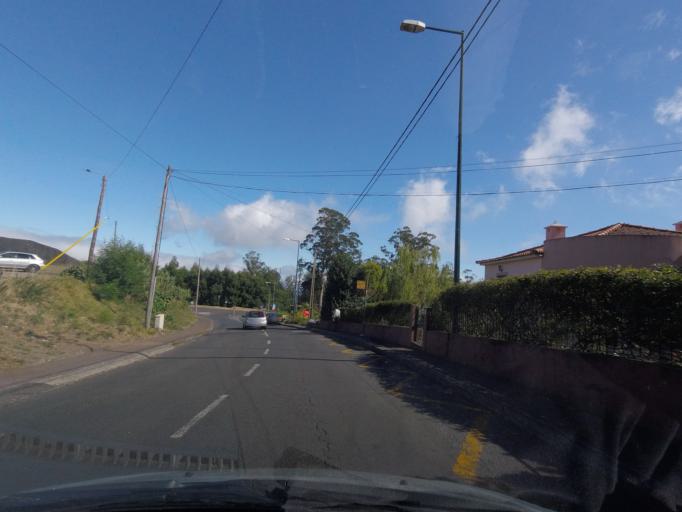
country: PT
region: Madeira
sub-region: Santa Cruz
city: Camacha
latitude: 32.6781
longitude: -16.8456
